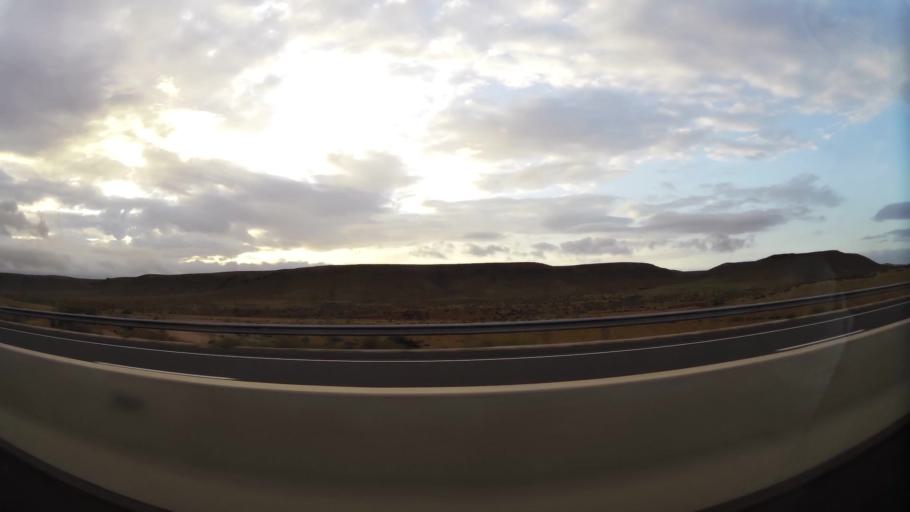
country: MA
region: Oriental
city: Taourirt
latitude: 34.4469
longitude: -3.0564
